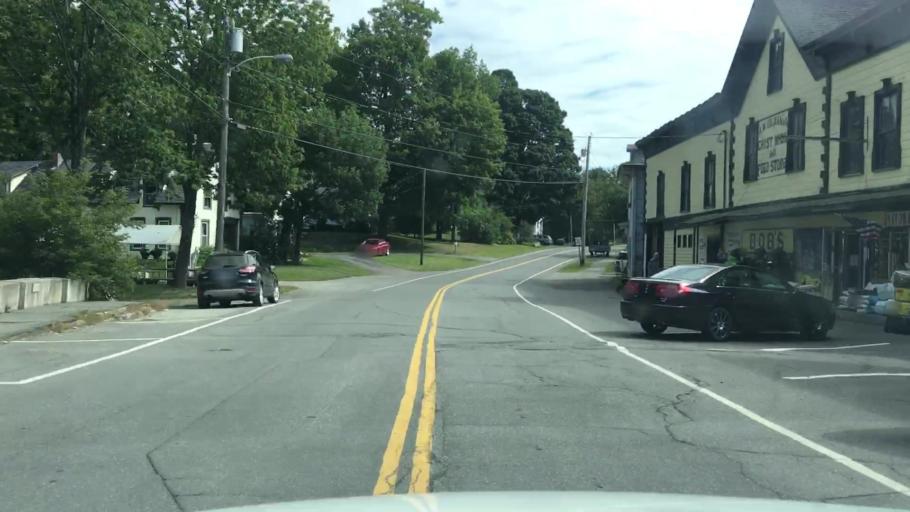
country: US
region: Maine
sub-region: Piscataquis County
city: Dover-Foxcroft
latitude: 45.1847
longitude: -69.2305
